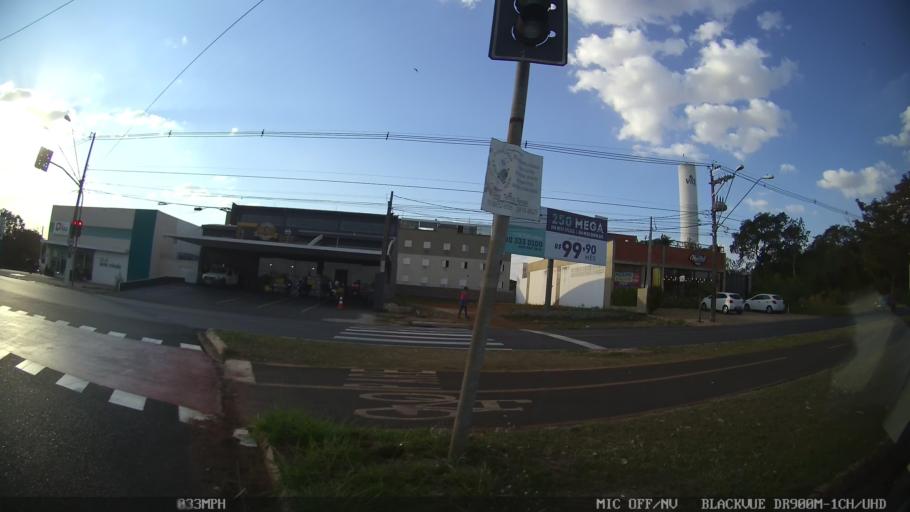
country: BR
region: Sao Paulo
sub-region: Ribeirao Preto
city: Ribeirao Preto
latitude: -21.1936
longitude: -47.7491
